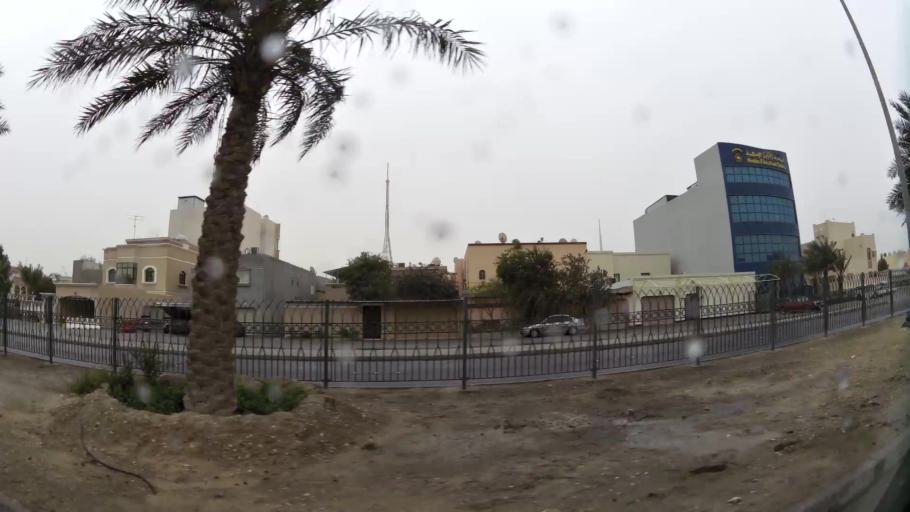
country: BH
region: Northern
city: Madinat `Isa
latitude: 26.1675
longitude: 50.5584
